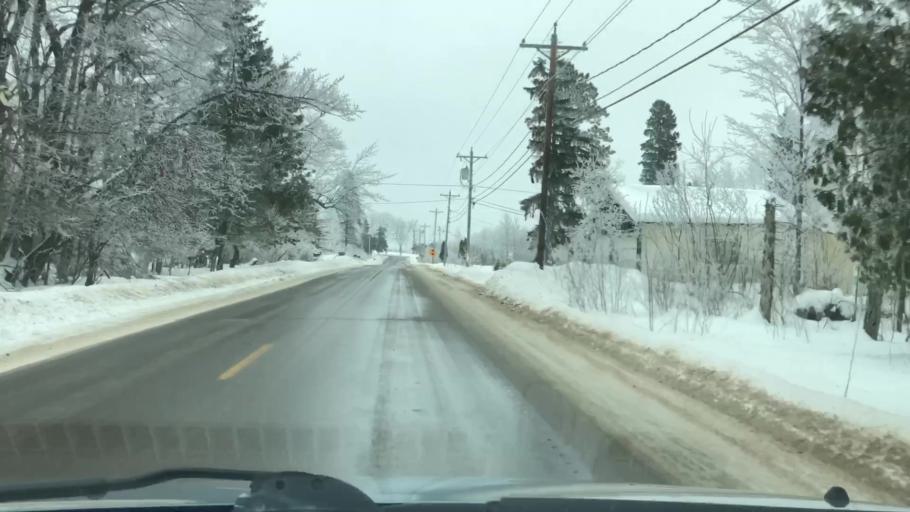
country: US
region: Minnesota
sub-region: Saint Louis County
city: Arnold
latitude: 46.8595
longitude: -92.1148
